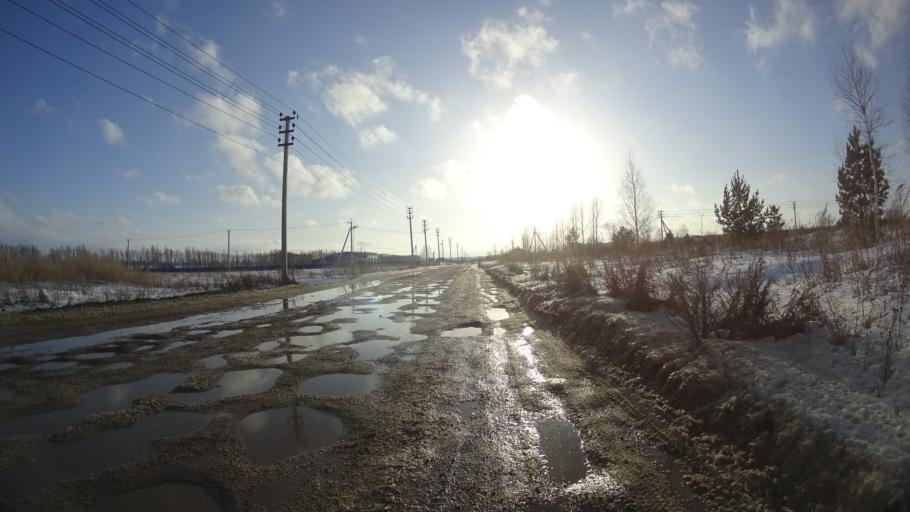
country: RU
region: Chelyabinsk
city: Sargazy
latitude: 55.1087
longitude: 61.2726
